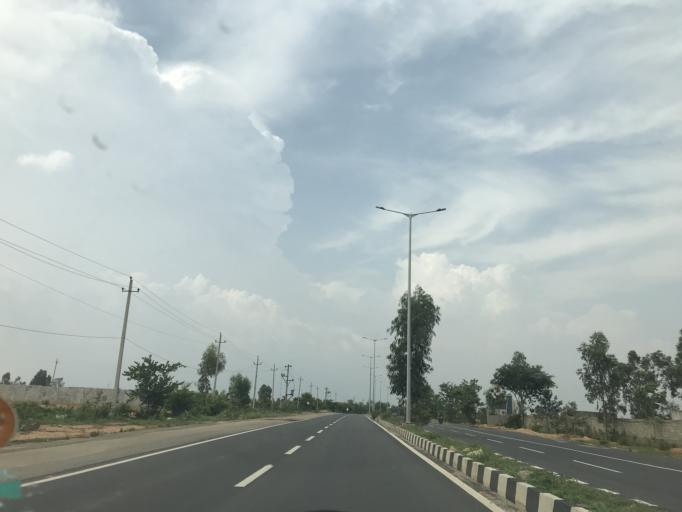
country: IN
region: Karnataka
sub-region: Bangalore Urban
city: Yelahanka
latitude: 13.1511
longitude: 77.6761
